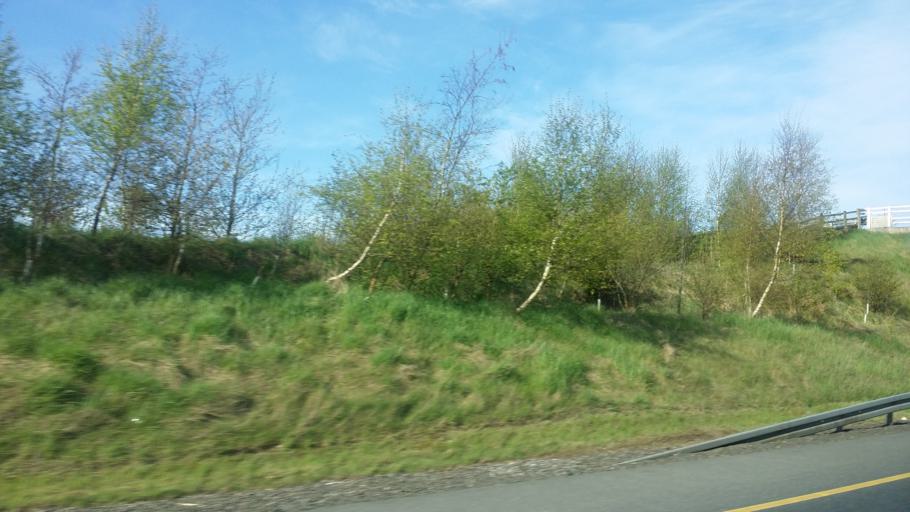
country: IE
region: Leinster
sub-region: An Mhi
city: Navan
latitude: 53.6156
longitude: -6.6696
